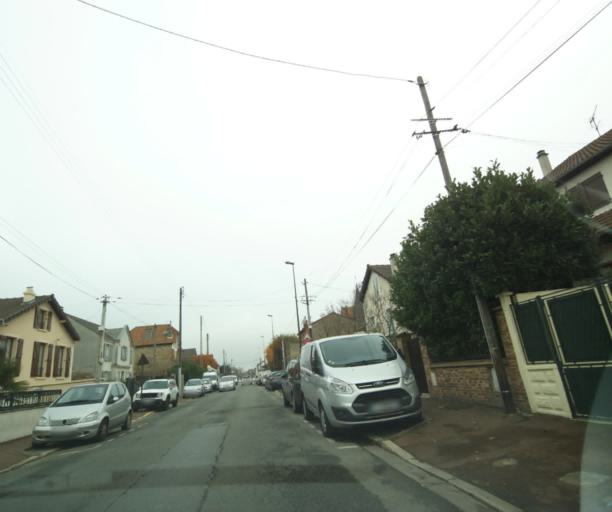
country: FR
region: Ile-de-France
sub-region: Departement de Seine-Saint-Denis
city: Le Raincy
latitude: 48.9159
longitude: 2.5214
